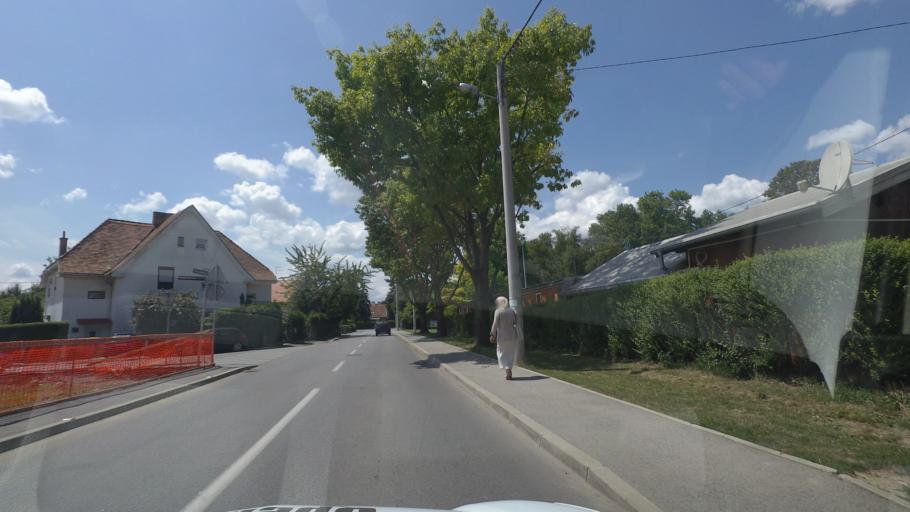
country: HR
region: Grad Zagreb
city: Dubrava
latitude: 45.8171
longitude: 16.0250
